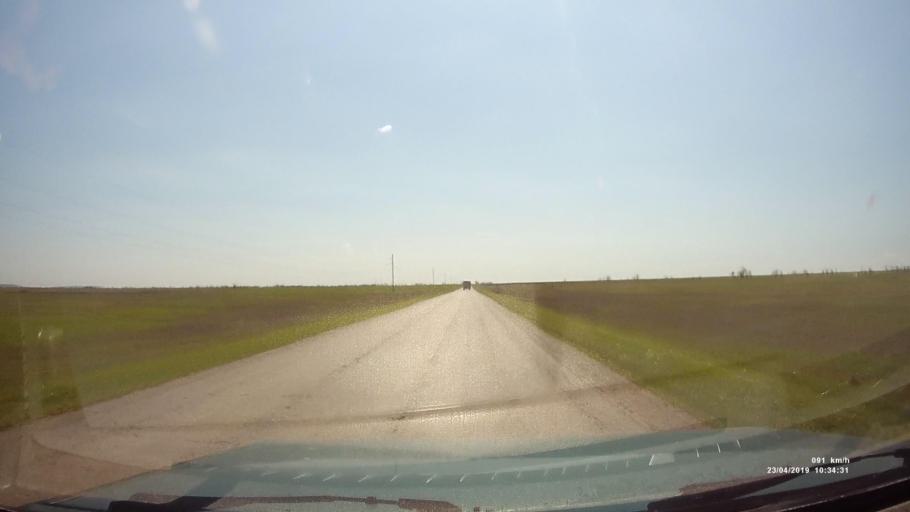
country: RU
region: Kalmykiya
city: Yashalta
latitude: 46.5632
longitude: 42.6114
